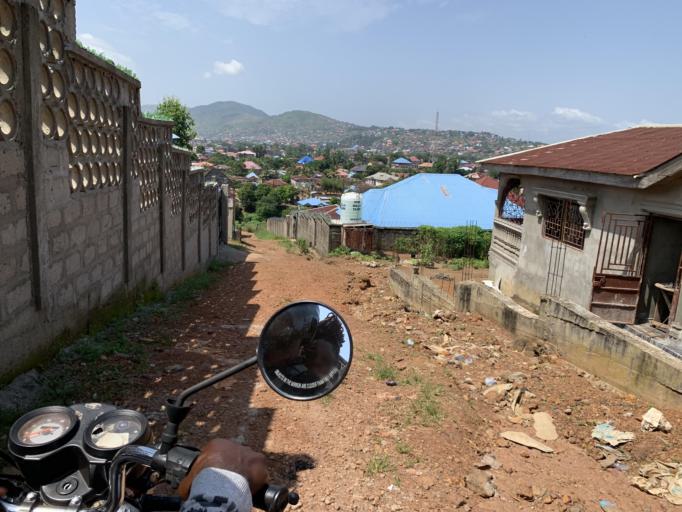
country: SL
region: Western Area
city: Hastings
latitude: 8.3821
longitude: -13.1456
